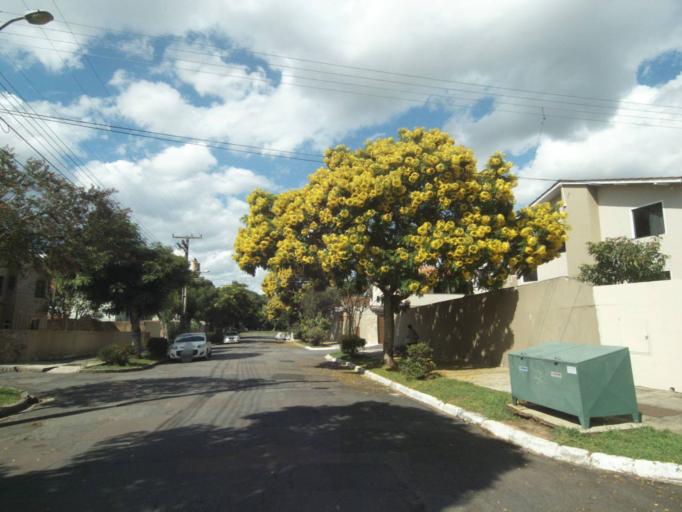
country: BR
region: Parana
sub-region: Curitiba
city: Curitiba
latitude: -25.4376
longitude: -49.3460
